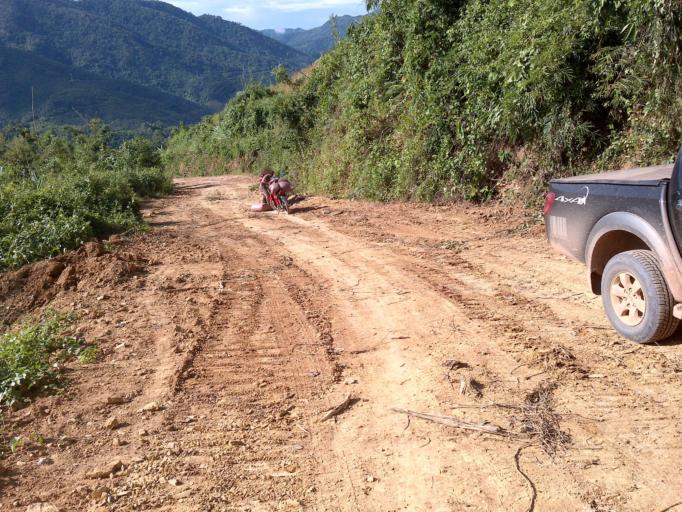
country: TH
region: Nan
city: Chaloem Phra Kiat
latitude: 19.9293
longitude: 101.1639
